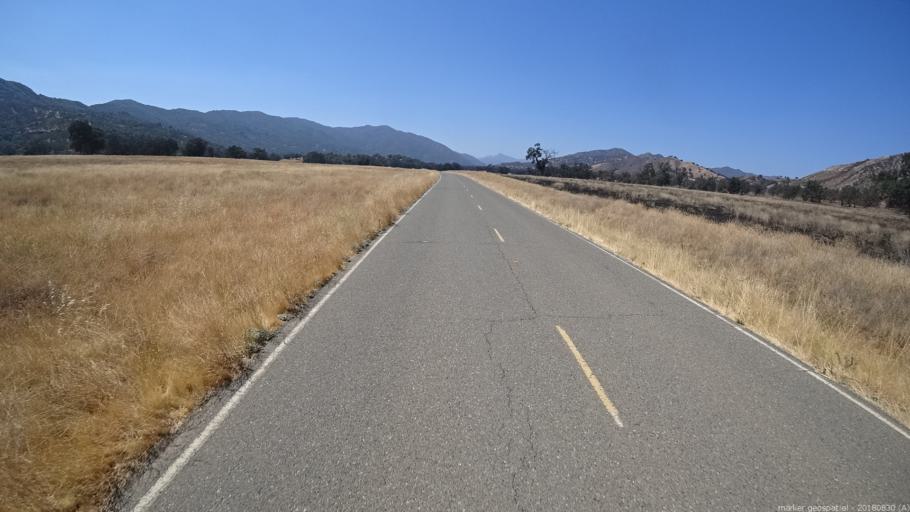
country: US
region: California
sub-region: Monterey County
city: King City
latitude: 35.9689
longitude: -121.3123
